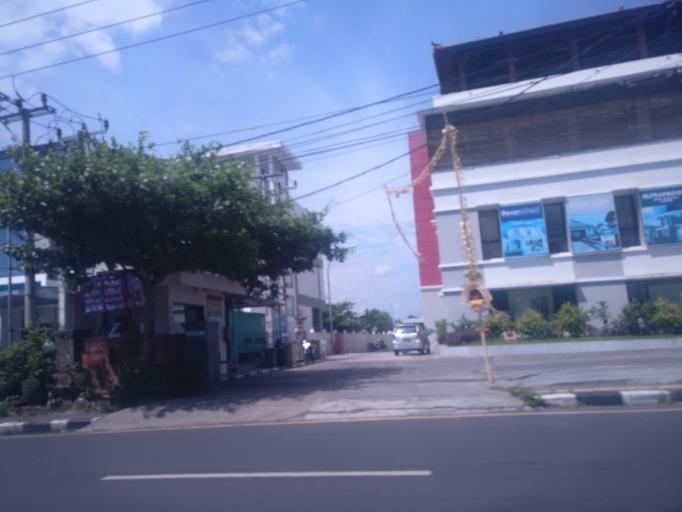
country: ID
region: Bali
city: Banjar Kertasari
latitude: -8.6364
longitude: 115.1954
